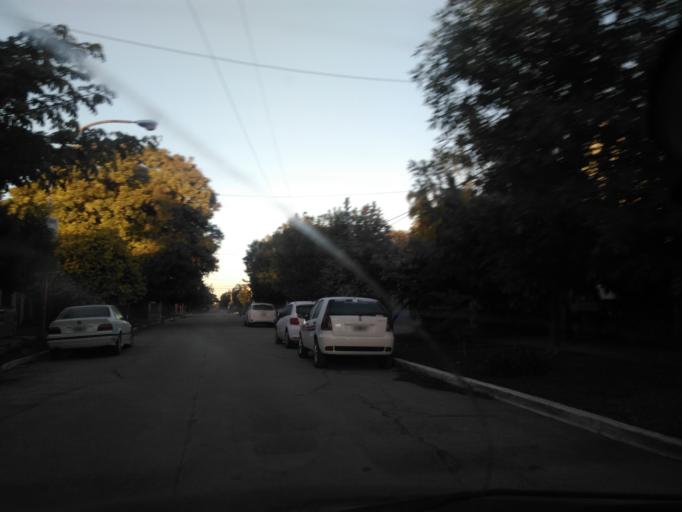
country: AR
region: Chaco
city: Resistencia
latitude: -27.4639
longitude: -58.9938
